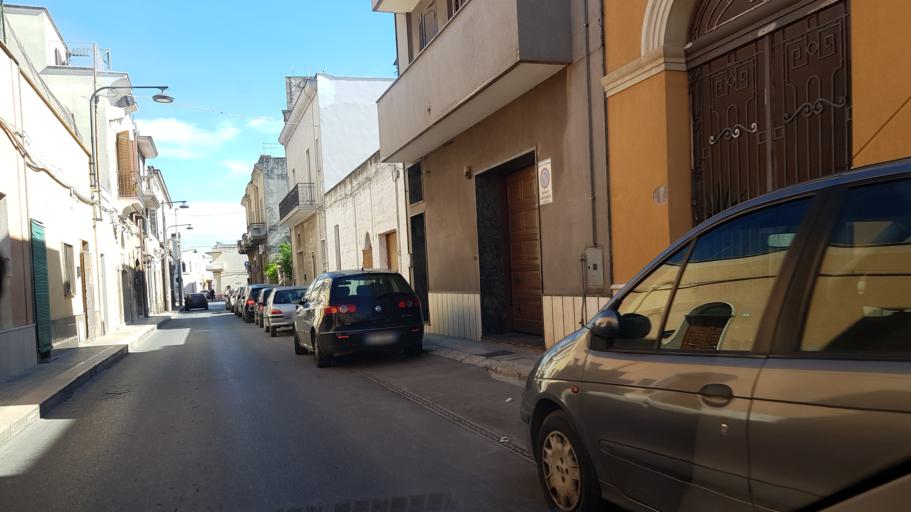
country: IT
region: Apulia
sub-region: Provincia di Brindisi
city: San Vito dei Normanni
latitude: 40.6575
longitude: 17.7069
